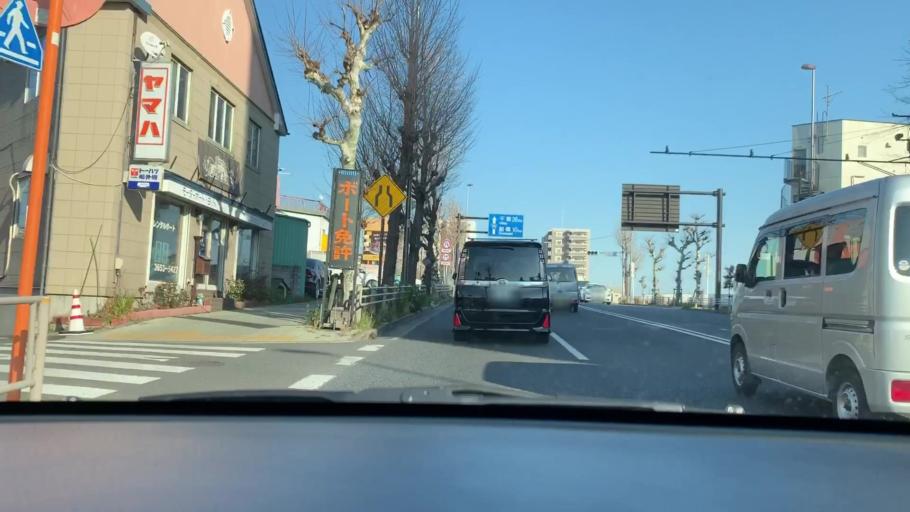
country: JP
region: Tokyo
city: Urayasu
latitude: 35.7025
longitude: 139.8830
